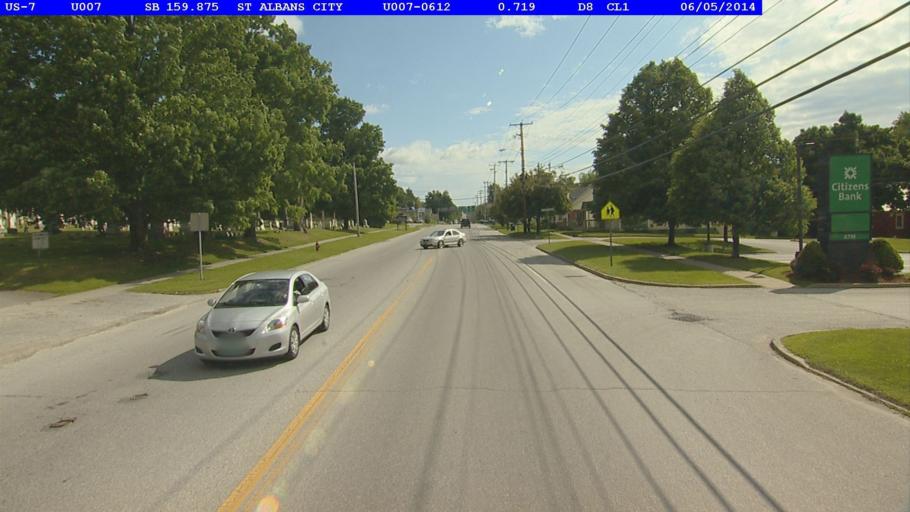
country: US
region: Vermont
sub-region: Franklin County
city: Saint Albans
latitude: 44.8038
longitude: -73.0871
